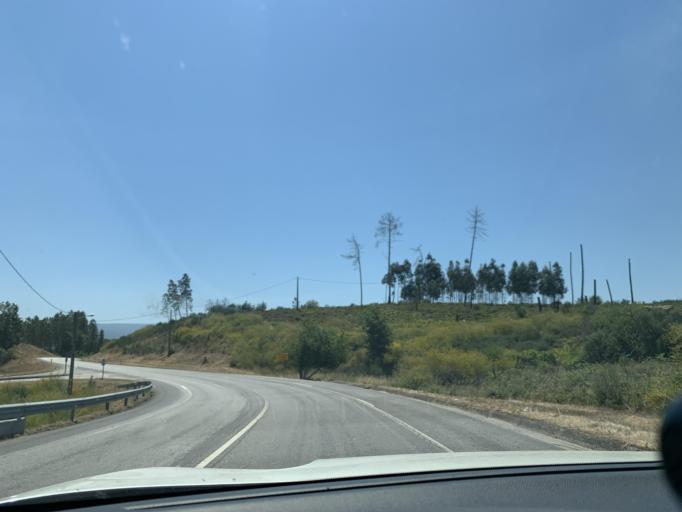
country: PT
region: Viseu
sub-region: Mangualde
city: Mangualde
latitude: 40.5683
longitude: -7.7232
